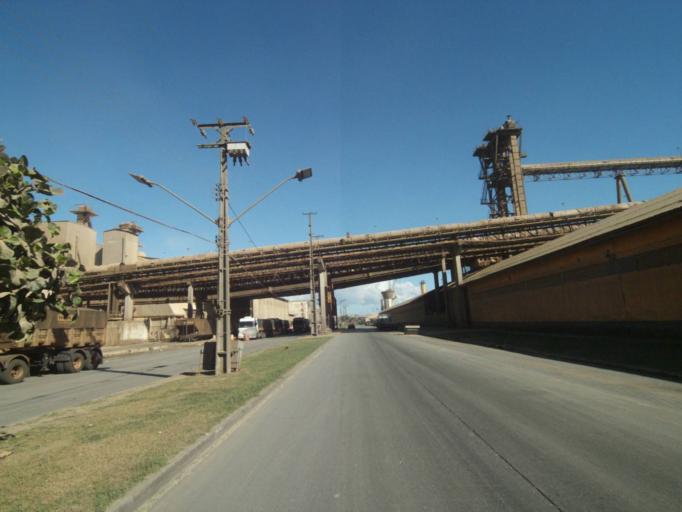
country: BR
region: Parana
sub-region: Paranagua
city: Paranagua
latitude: -25.5030
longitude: -48.5069
